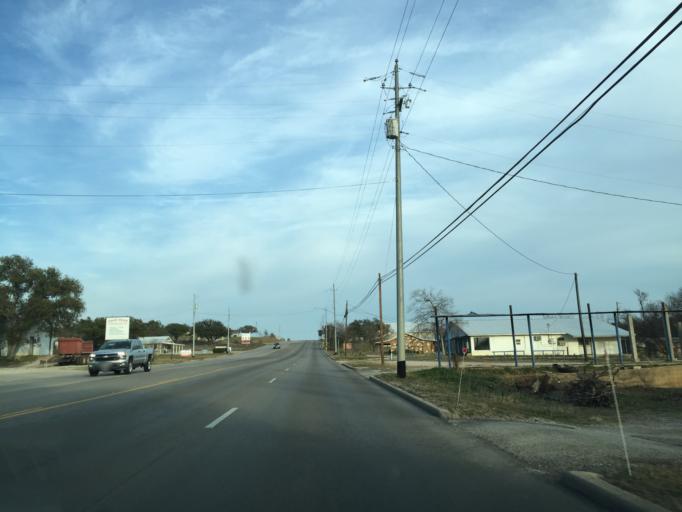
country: US
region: Texas
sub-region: Llano County
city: Llano
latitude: 30.7594
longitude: -98.6688
